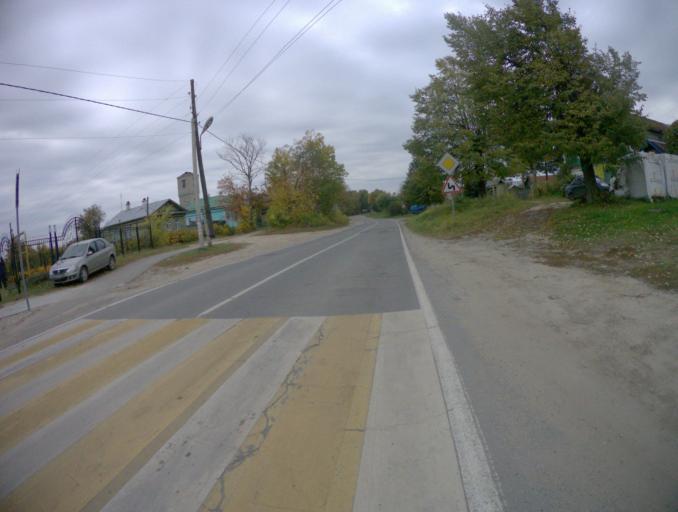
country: RU
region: Vladimir
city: Mstera
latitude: 56.3804
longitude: 41.9300
